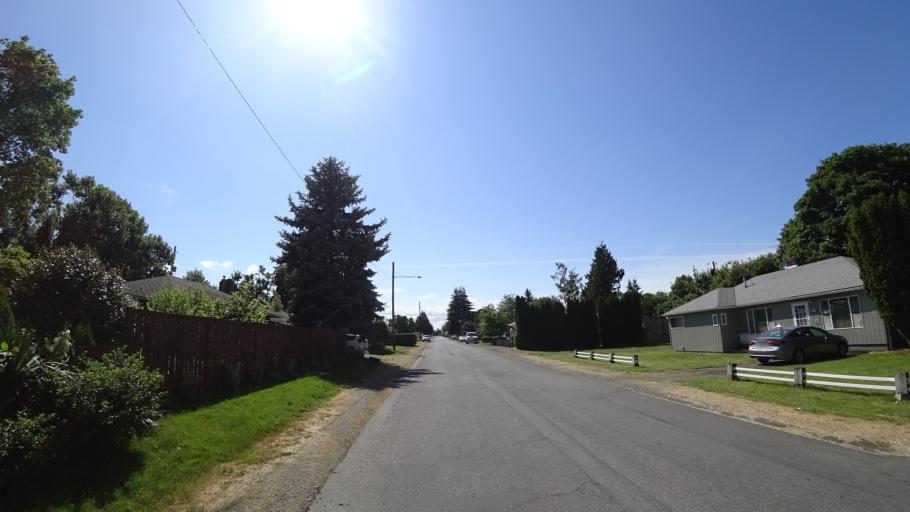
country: US
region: Oregon
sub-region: Multnomah County
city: Lents
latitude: 45.5592
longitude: -122.5744
